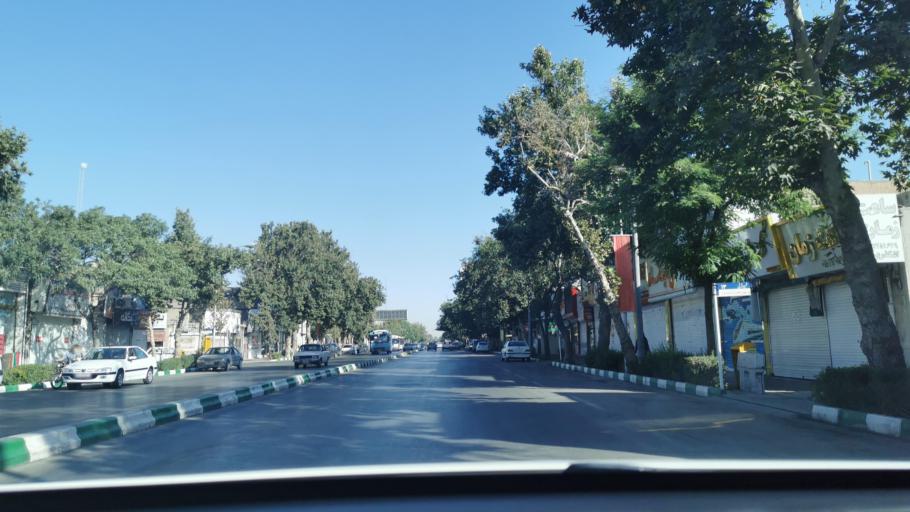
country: IR
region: Razavi Khorasan
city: Mashhad
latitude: 36.3090
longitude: 59.5942
